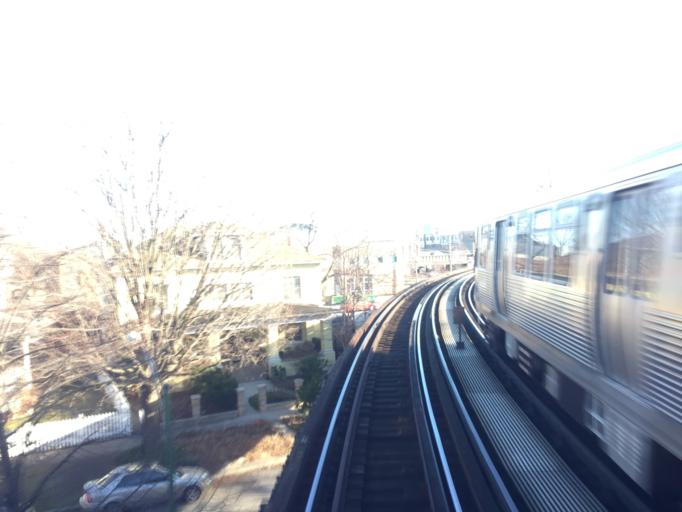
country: US
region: Illinois
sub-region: Cook County
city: Lincolnwood
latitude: 41.9662
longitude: -87.6763
